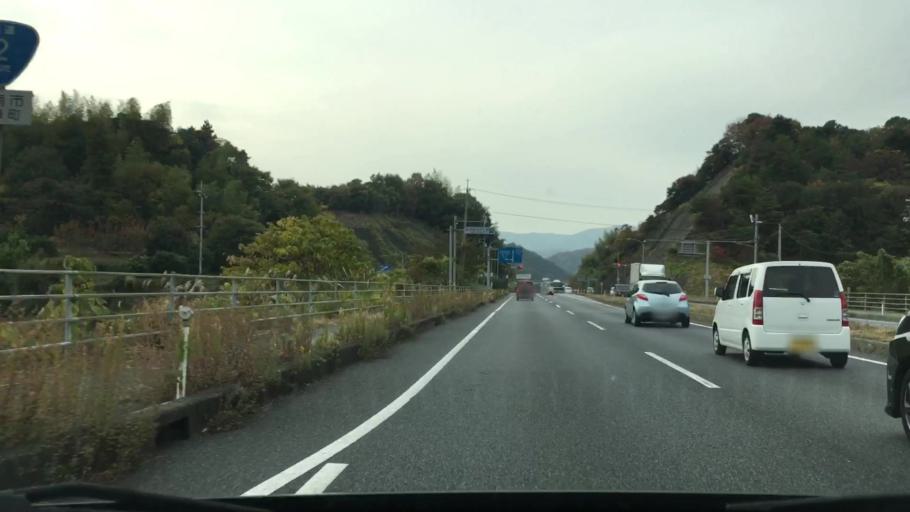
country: JP
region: Yamaguchi
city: Tokuyama
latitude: 34.0771
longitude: 131.7326
